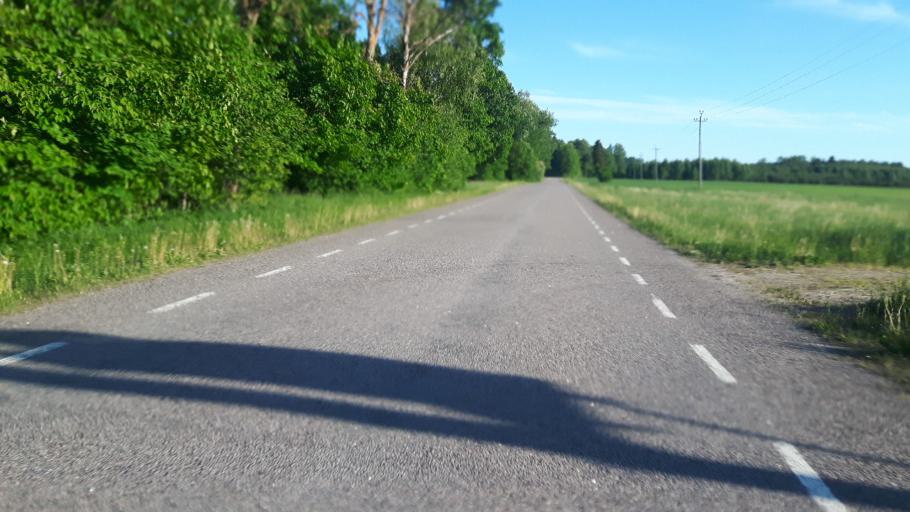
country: EE
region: Raplamaa
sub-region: Kehtna vald
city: Kehtna
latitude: 58.8949
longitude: 24.8797
